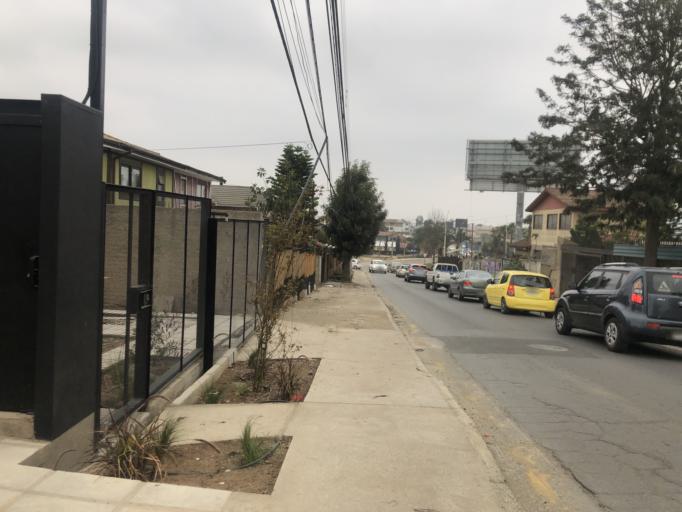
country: CL
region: Valparaiso
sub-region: Provincia de Marga Marga
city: Quilpue
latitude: -33.0488
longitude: -71.4270
